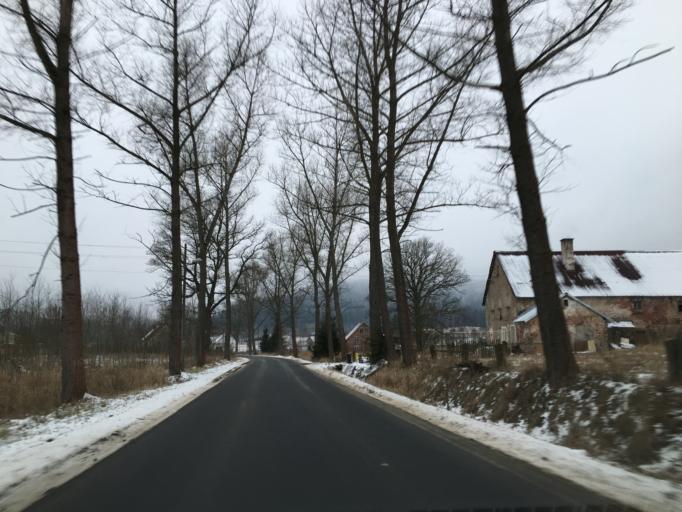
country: PL
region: Lower Silesian Voivodeship
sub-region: Powiat walbrzyski
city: Mieroszow
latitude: 50.6699
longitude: 16.1349
